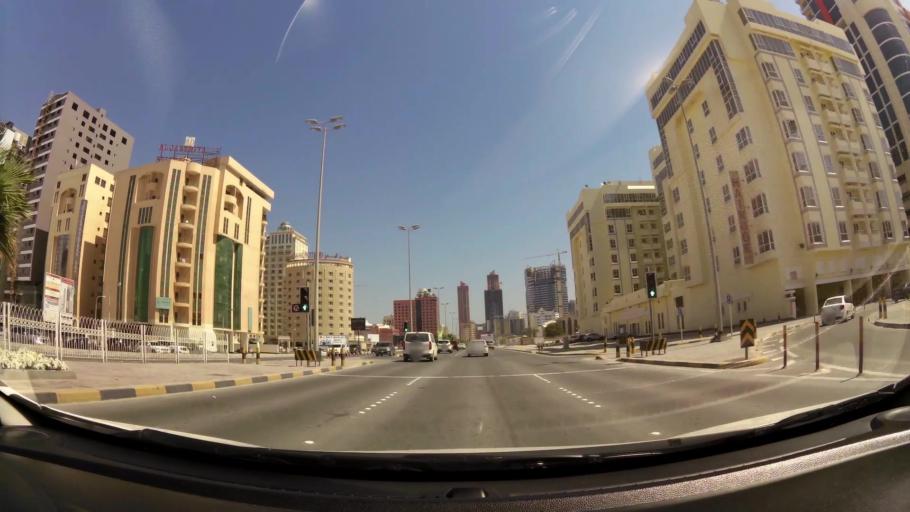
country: BH
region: Manama
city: Manama
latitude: 26.2166
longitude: 50.6028
